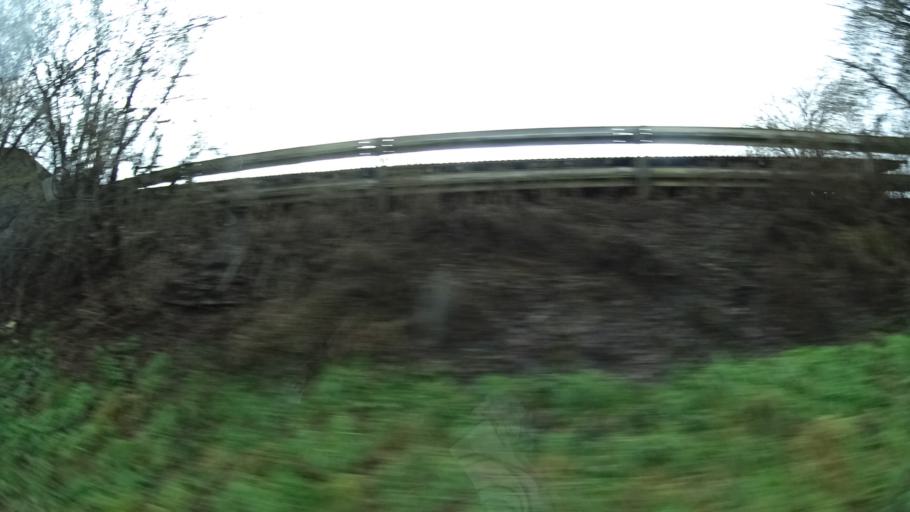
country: DE
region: Hesse
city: Tann
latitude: 50.6230
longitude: 10.0241
